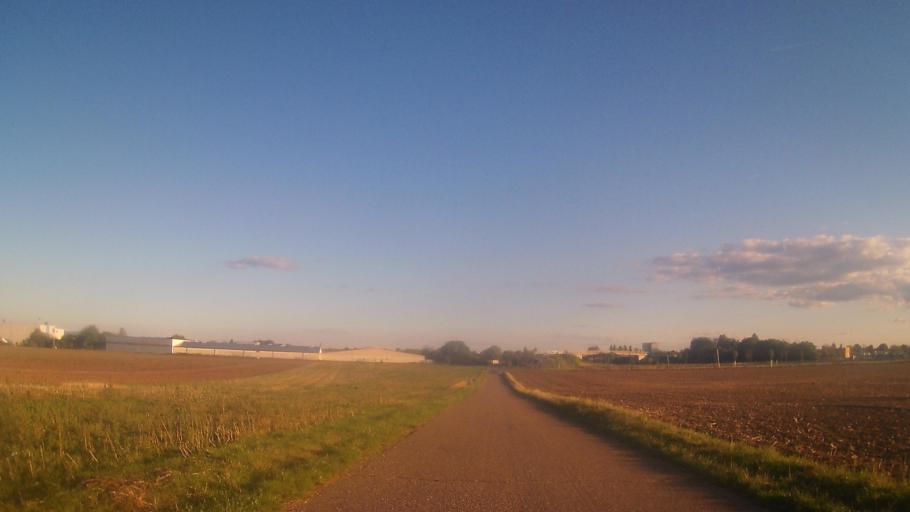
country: DE
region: Rheinland-Pfalz
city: Worms
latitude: 49.6200
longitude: 8.3422
